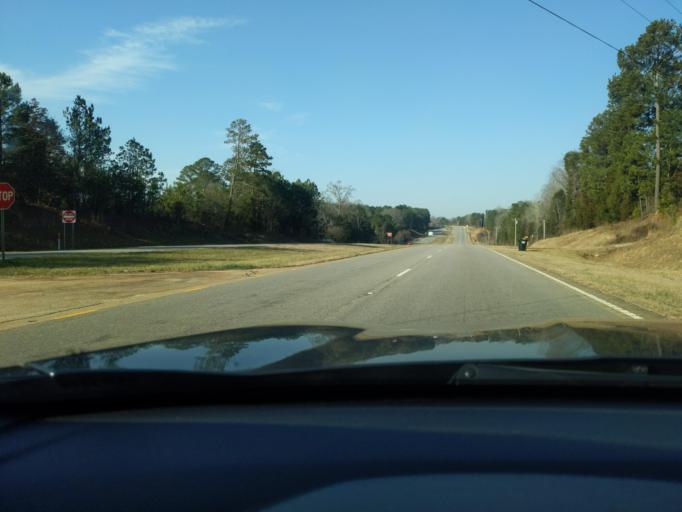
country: US
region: South Carolina
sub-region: Greenwood County
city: Greenwood
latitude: 34.1895
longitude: -82.2635
